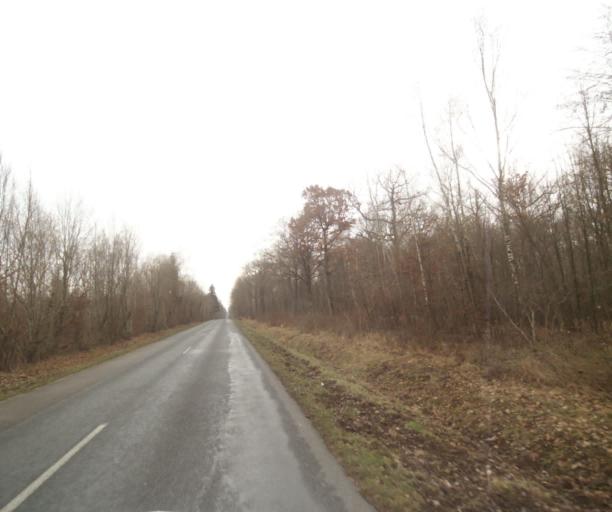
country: FR
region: Champagne-Ardenne
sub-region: Departement de la Marne
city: Pargny-sur-Saulx
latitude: 48.7225
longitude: 4.8742
